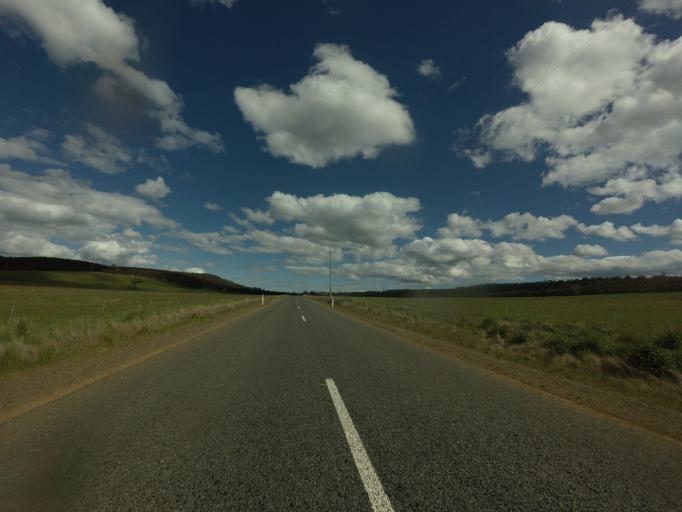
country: AU
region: Tasmania
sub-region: Brighton
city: Bridgewater
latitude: -42.4501
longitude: 147.3118
